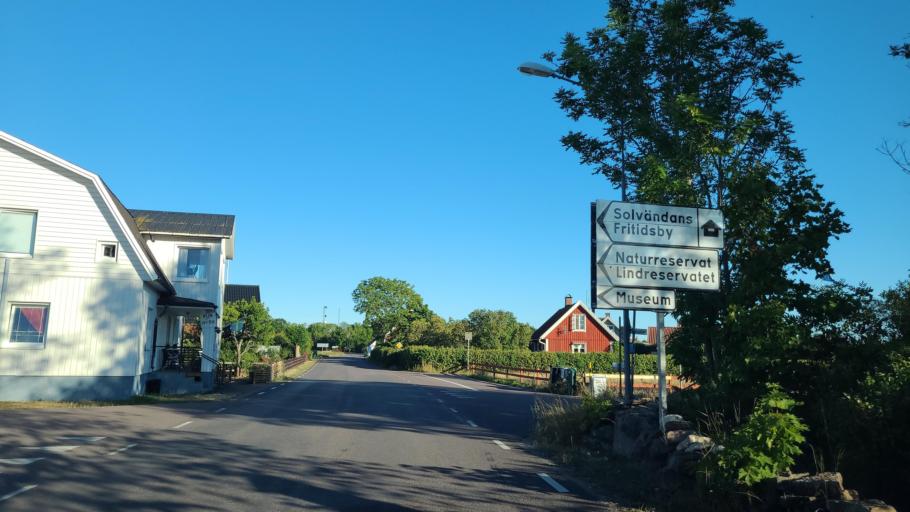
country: SE
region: Kalmar
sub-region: Borgholms Kommun
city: Borgholm
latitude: 57.3175
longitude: 17.0171
